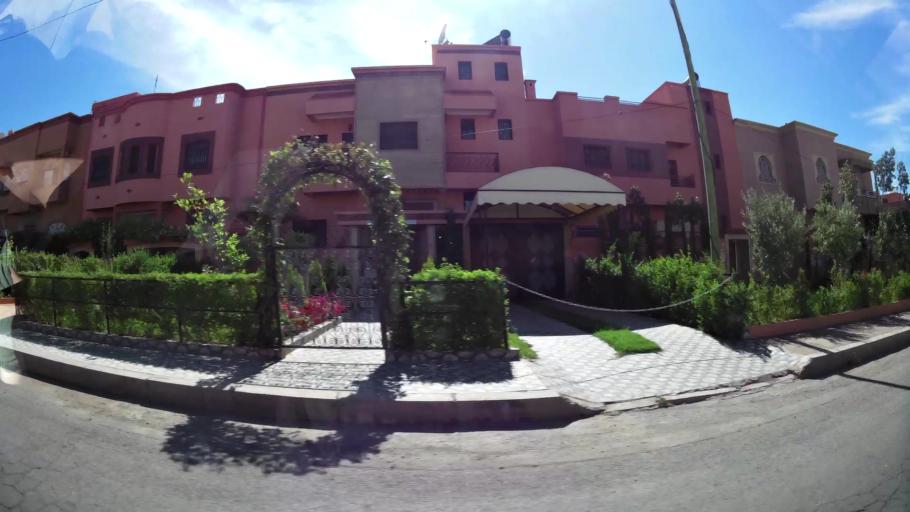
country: MA
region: Marrakech-Tensift-Al Haouz
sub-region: Marrakech
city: Marrakesh
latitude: 31.6375
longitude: -8.0391
